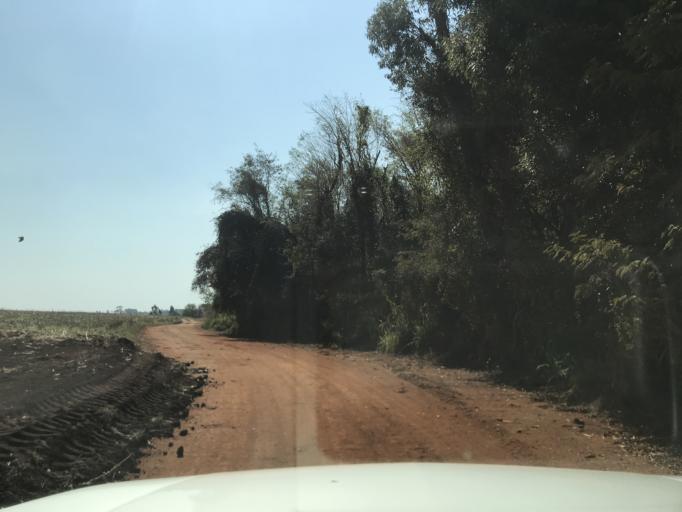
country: BR
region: Parana
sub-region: Palotina
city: Palotina
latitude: -24.2192
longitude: -53.7338
